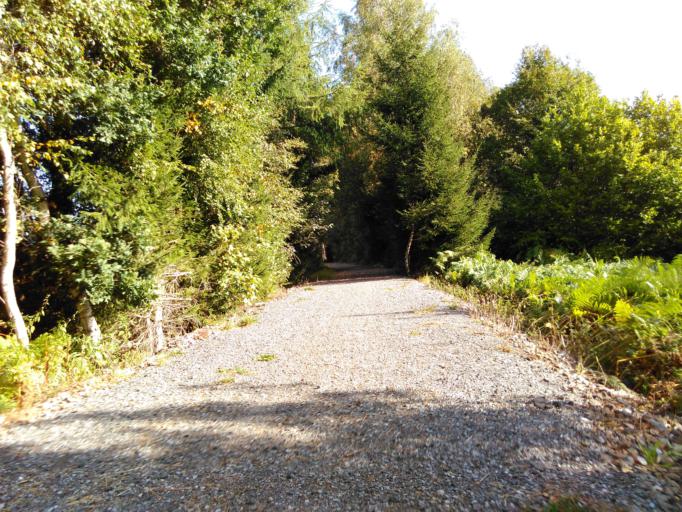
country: BE
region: Wallonia
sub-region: Province du Luxembourg
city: Neufchateau
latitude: 49.9133
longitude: 5.3949
